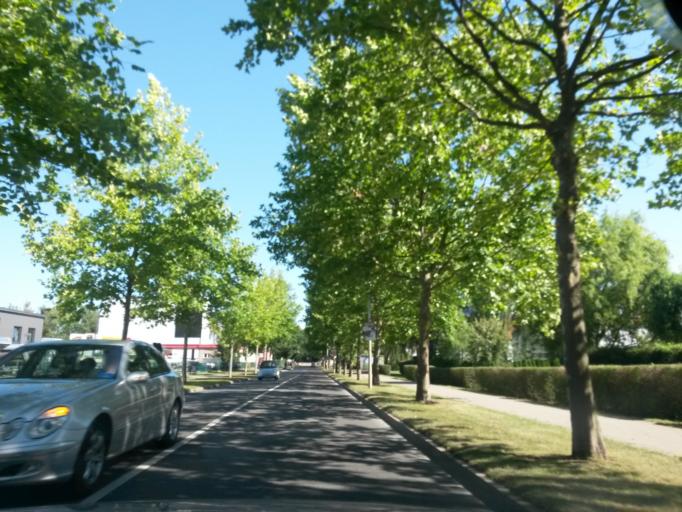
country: DE
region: Brandenburg
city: Prenzlau
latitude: 53.3032
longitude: 13.8232
